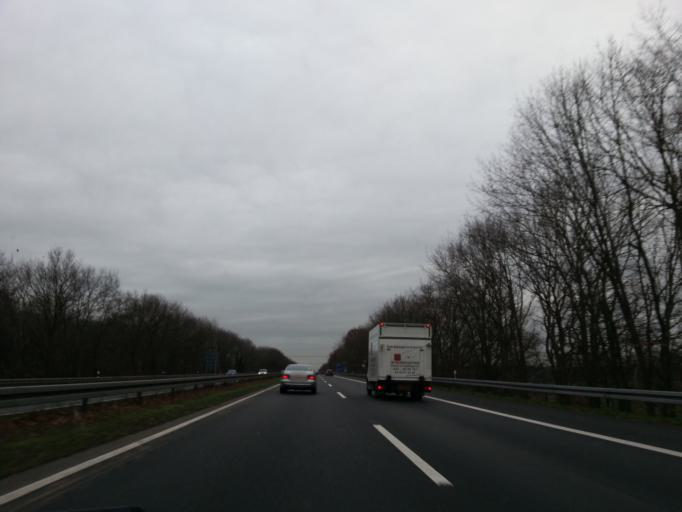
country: DE
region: North Rhine-Westphalia
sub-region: Regierungsbezirk Dusseldorf
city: Hunxe
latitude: 51.6693
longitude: 6.7172
